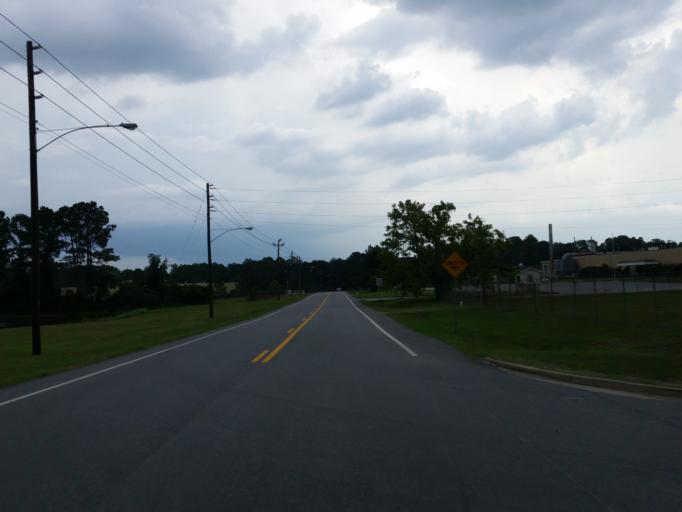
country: US
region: Georgia
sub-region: Tift County
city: Unionville
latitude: 31.4171
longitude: -83.4937
